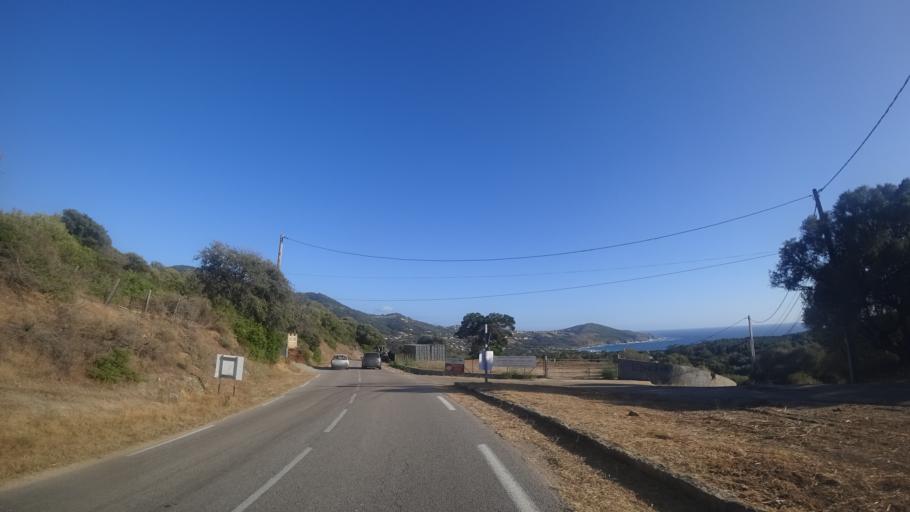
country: FR
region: Corsica
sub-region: Departement de la Corse-du-Sud
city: Cargese
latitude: 42.1610
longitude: 8.5968
